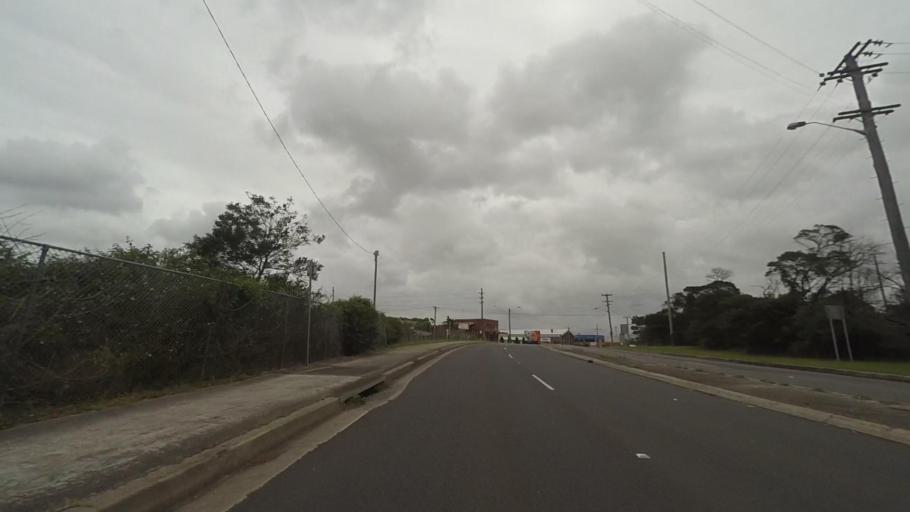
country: AU
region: New South Wales
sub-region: Wollongong
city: Berkeley
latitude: -34.4650
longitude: 150.8354
